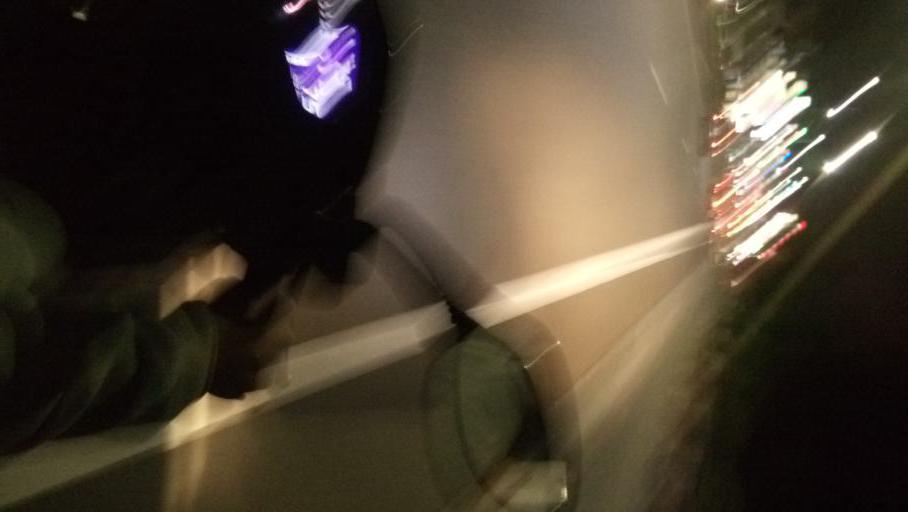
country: TW
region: Taiwan
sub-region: Hsinchu
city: Zhubei
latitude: 24.7248
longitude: 121.1327
